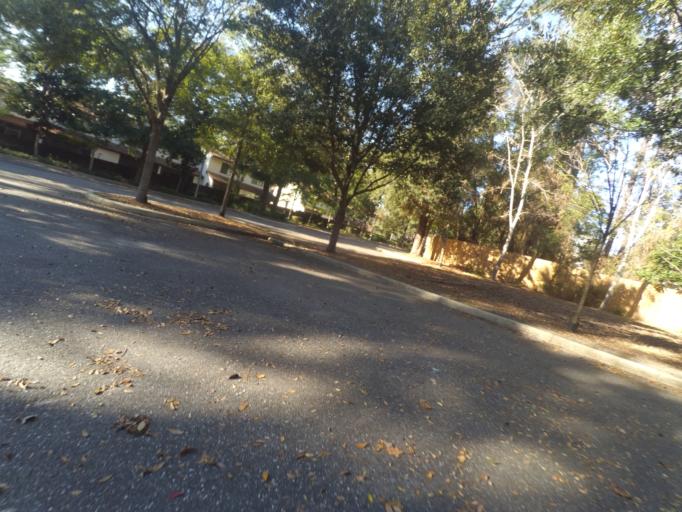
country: US
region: Florida
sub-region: Alachua County
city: Gainesville
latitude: 29.6184
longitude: -82.3601
